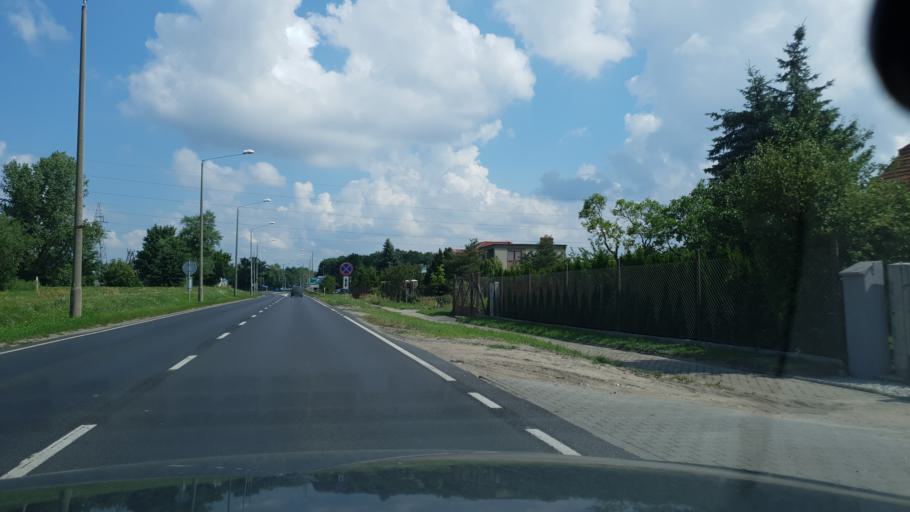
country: PL
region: Kujawsko-Pomorskie
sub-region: Grudziadz
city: Grudziadz
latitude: 53.4498
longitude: 18.7305
